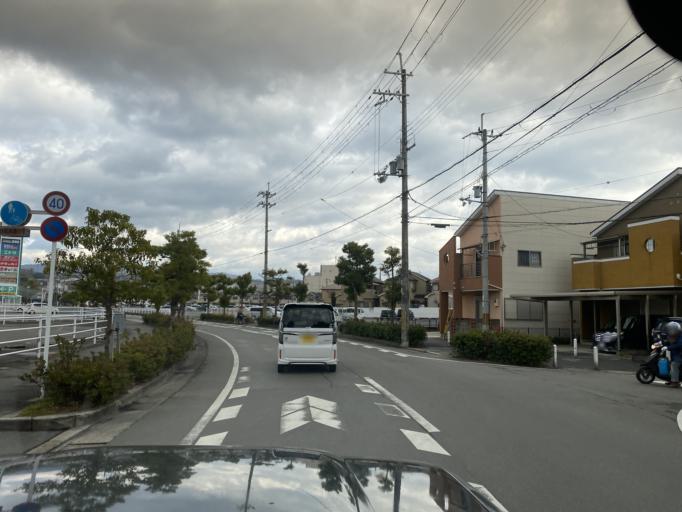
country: JP
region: Kyoto
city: Tanabe
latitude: 34.8407
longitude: 135.7854
